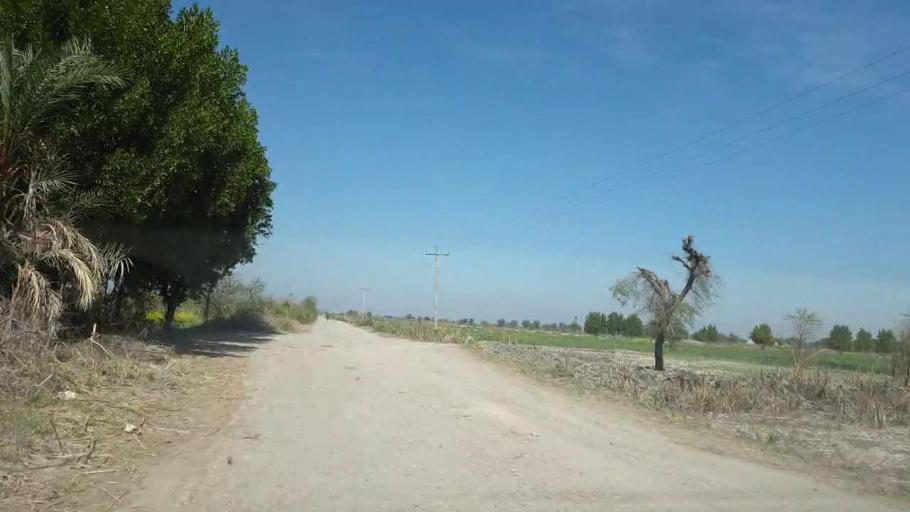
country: PK
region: Sindh
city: Pithoro
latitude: 25.6148
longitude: 69.2162
